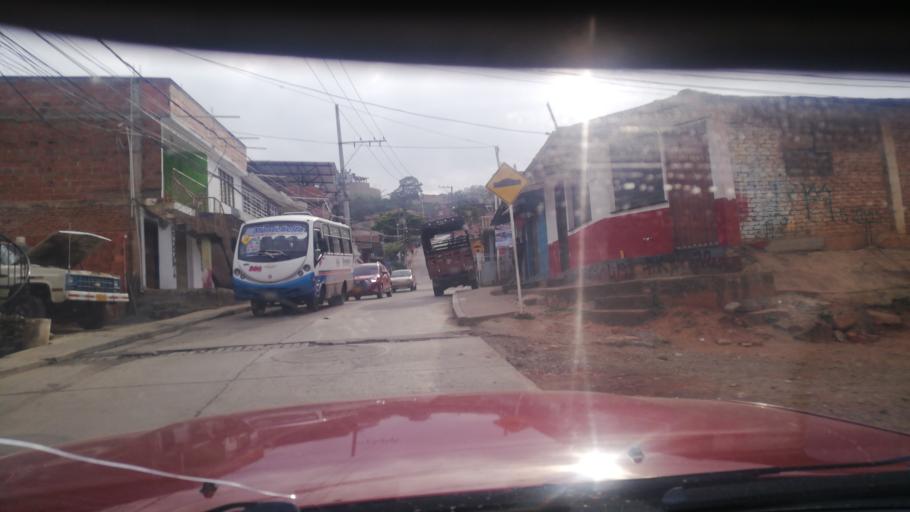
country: CO
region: Valle del Cauca
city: Cali
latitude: 3.4845
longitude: -76.5516
